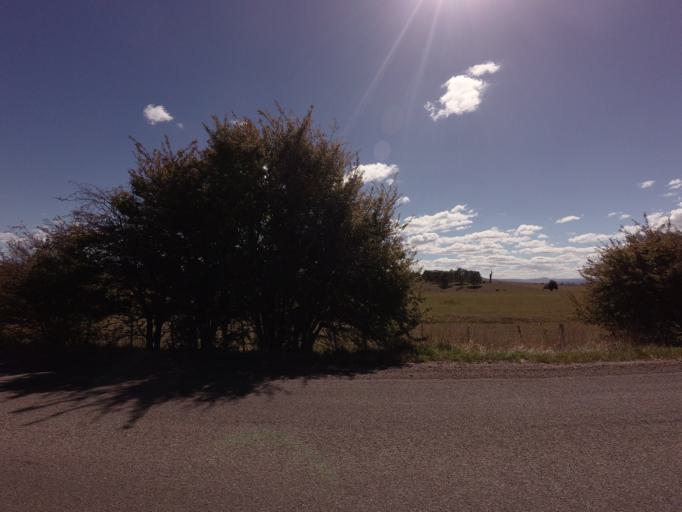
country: AU
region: Tasmania
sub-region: Break O'Day
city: St Helens
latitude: -41.6267
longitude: 147.9920
